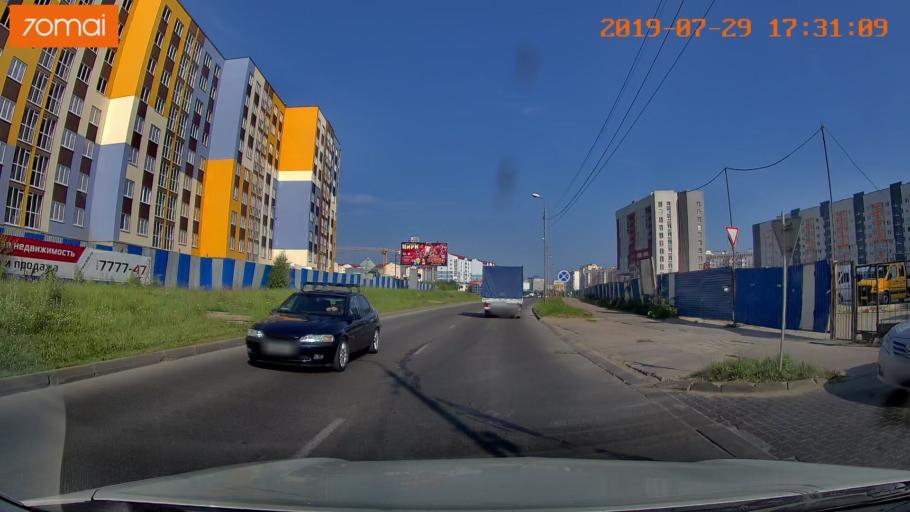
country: RU
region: Kaliningrad
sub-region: Gorod Kaliningrad
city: Kaliningrad
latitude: 54.7482
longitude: 20.4847
